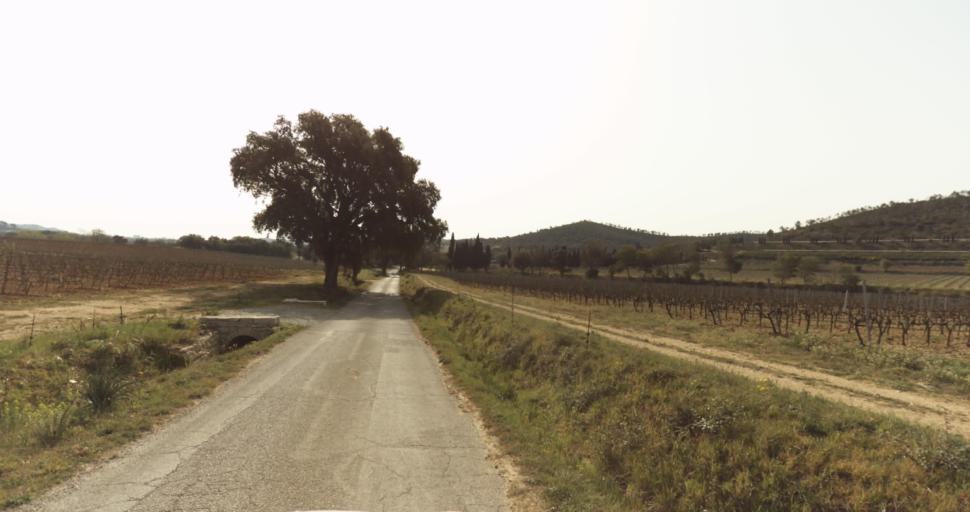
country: FR
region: Provence-Alpes-Cote d'Azur
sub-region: Departement du Var
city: Bormes-les-Mimosas
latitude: 43.1445
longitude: 6.3094
